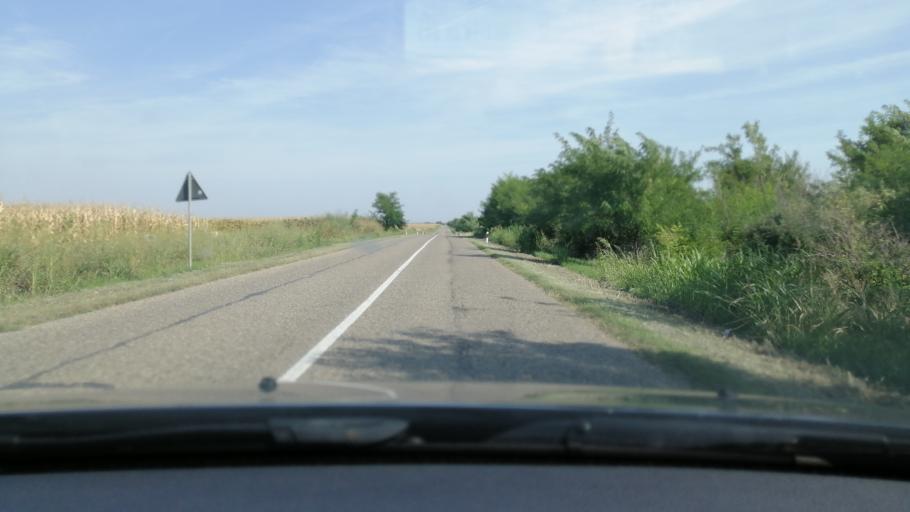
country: RS
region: Autonomna Pokrajina Vojvodina
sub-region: Juznobanatski Okrug
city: Kovacica
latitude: 45.1575
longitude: 20.6171
